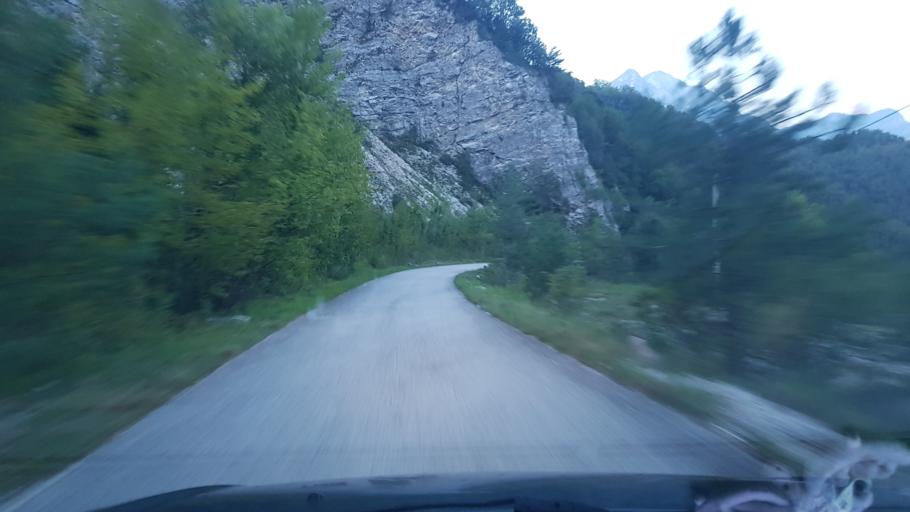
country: IT
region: Friuli Venezia Giulia
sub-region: Provincia di Pordenone
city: Frisanco
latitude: 46.2532
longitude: 12.7074
